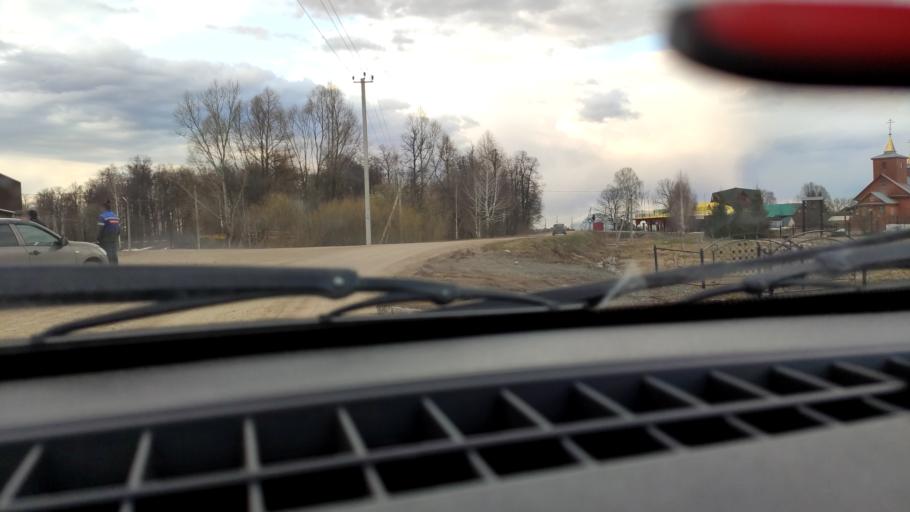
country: RU
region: Bashkortostan
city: Kudeyevskiy
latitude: 54.8127
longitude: 56.7528
